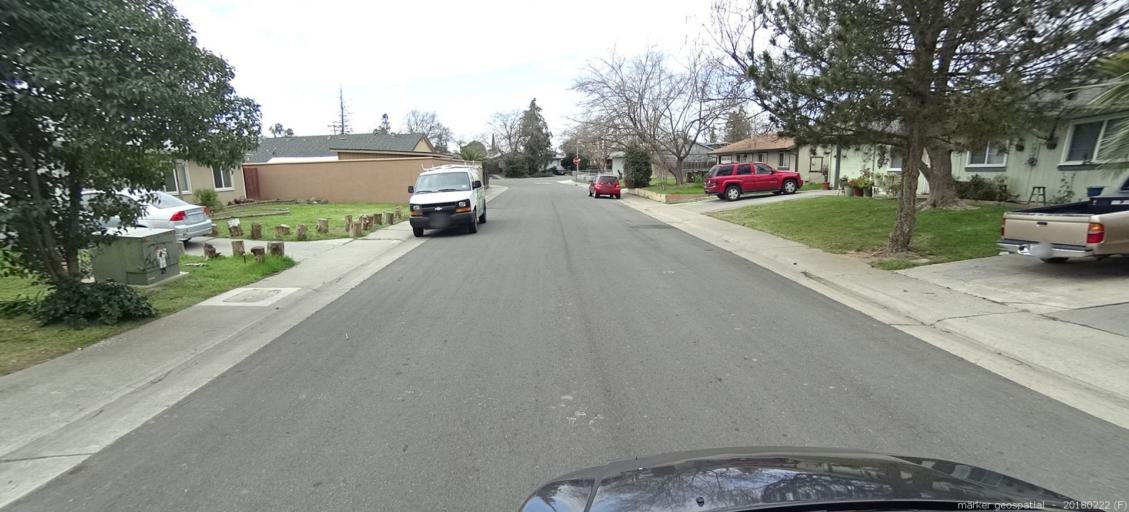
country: US
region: California
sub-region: Sacramento County
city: North Highlands
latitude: 38.7186
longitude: -121.4072
